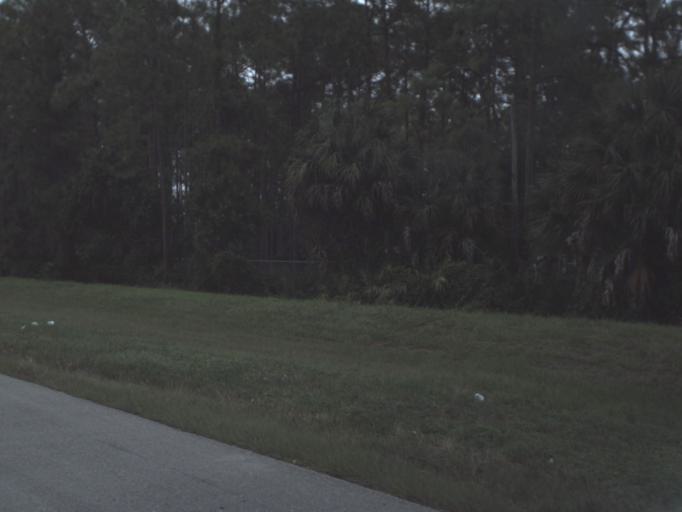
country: US
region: Florida
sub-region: Collier County
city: Vineyards
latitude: 26.2495
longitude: -81.7379
